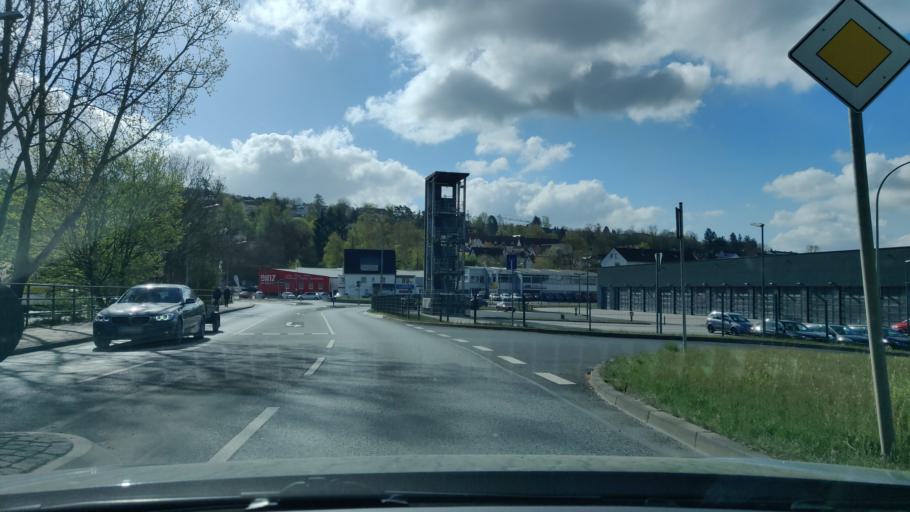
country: DE
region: Hesse
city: Melsungen
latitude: 51.1256
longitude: 9.5417
